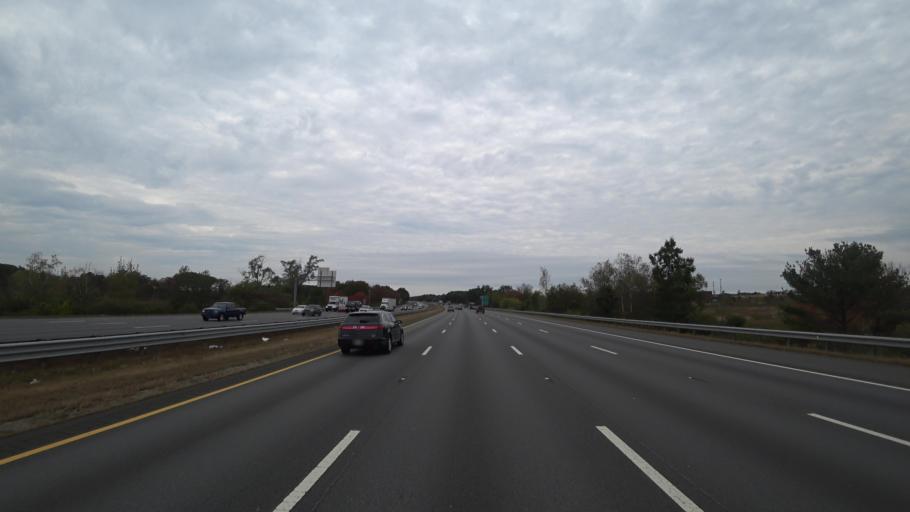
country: US
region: Massachusetts
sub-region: Middlesex County
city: Wilmington
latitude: 42.5500
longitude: -71.1367
